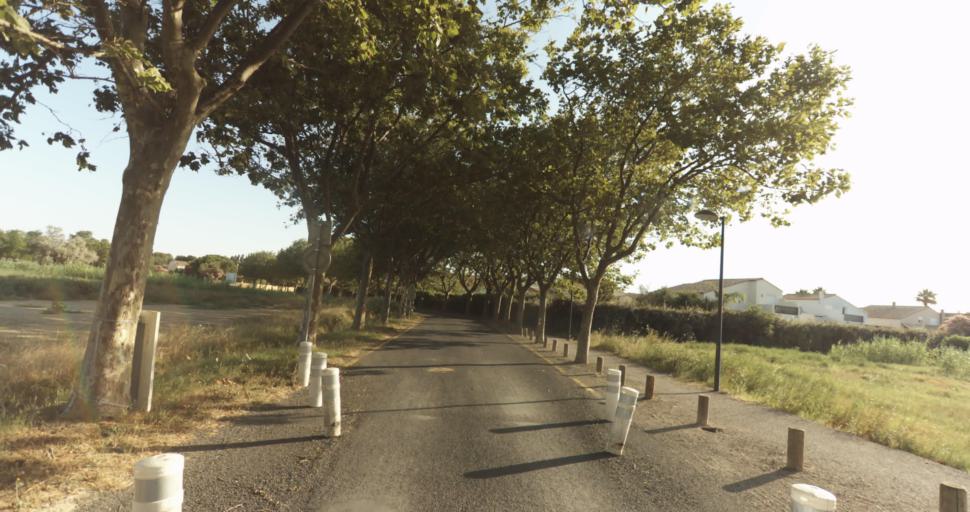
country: FR
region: Languedoc-Roussillon
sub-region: Departement des Pyrenees-Orientales
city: Latour-Bas-Elne
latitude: 42.5998
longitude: 3.0324
